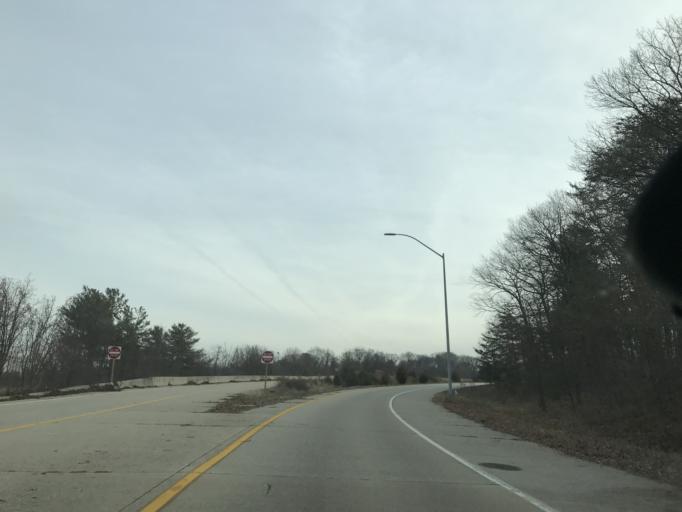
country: US
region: Maryland
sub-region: Prince George's County
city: Lanham
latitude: 38.9513
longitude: -76.8654
